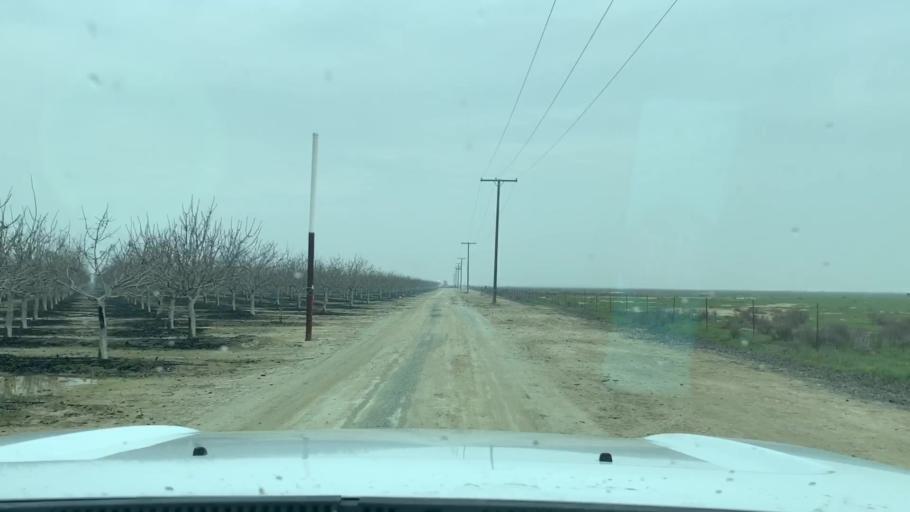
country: US
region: California
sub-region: Tulare County
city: Earlimart
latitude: 35.8372
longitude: -119.3398
